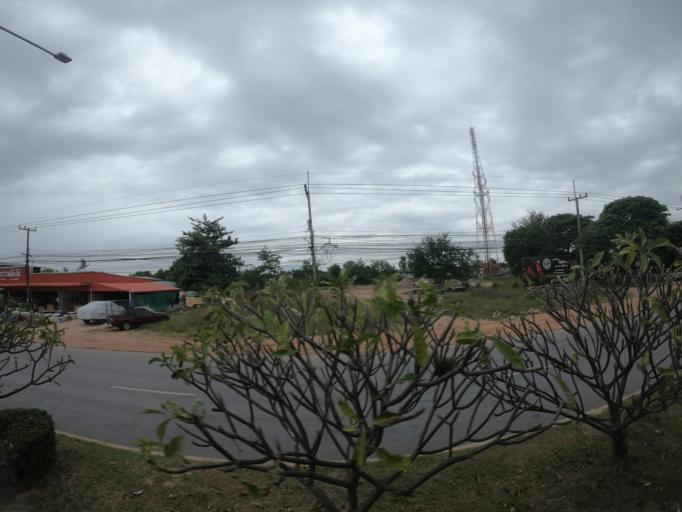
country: TH
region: Maha Sarakham
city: Maha Sarakham
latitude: 16.1756
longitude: 103.2958
